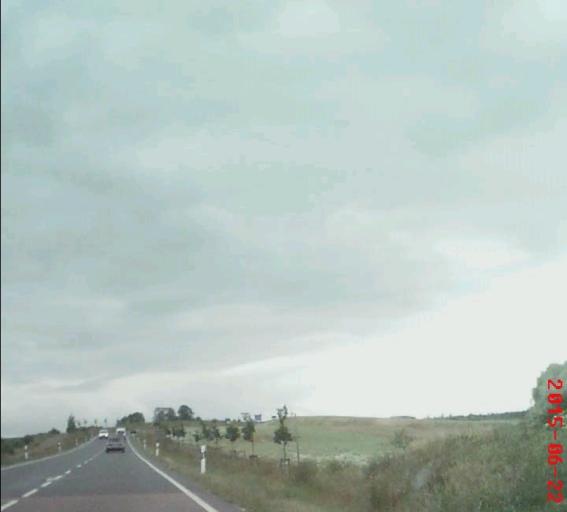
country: DE
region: Saxony-Anhalt
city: Zscherben
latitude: 51.4555
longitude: 11.8767
